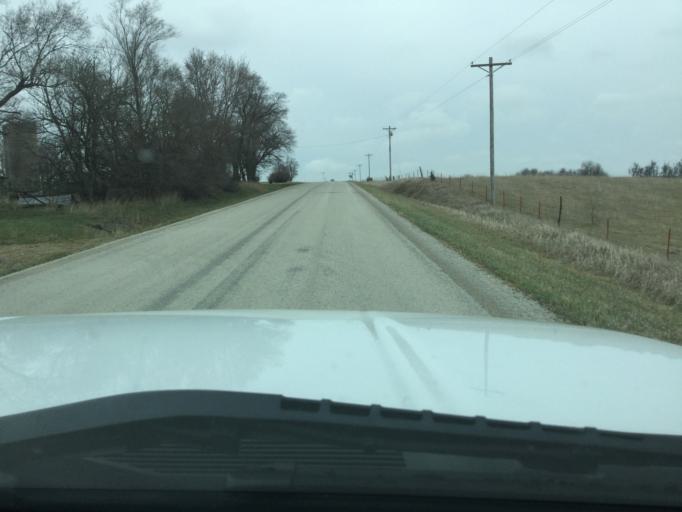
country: US
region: Kansas
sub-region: Nemaha County
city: Sabetha
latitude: 39.8753
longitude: -95.7140
